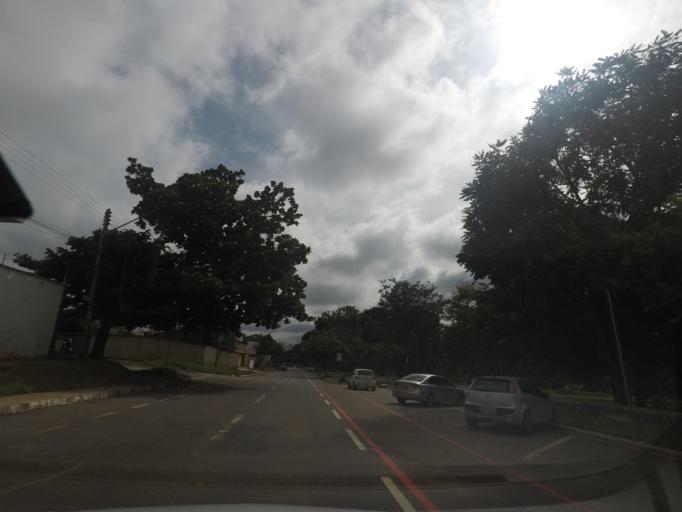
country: BR
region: Goias
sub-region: Goiania
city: Goiania
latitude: -16.7227
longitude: -49.2520
